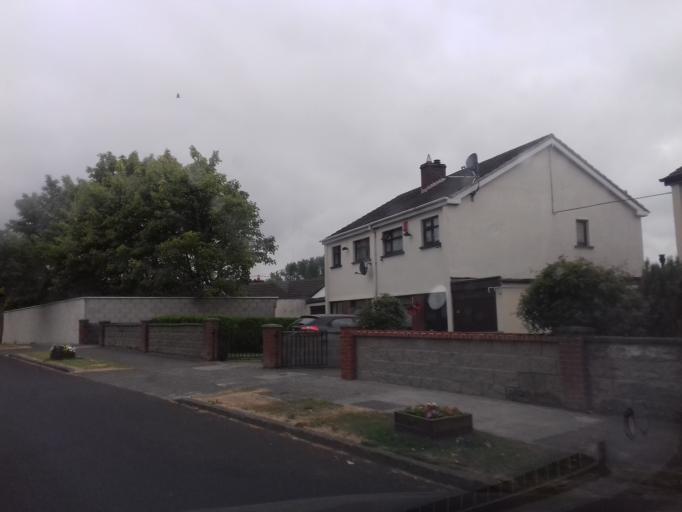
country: IE
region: Leinster
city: Hartstown
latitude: 53.3978
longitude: -6.4055
